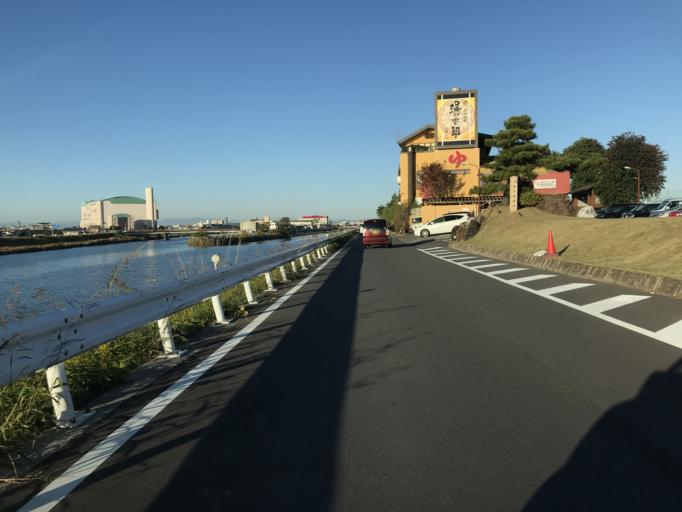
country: JP
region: Aichi
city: Nagoya-shi
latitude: 35.1821
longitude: 136.8448
